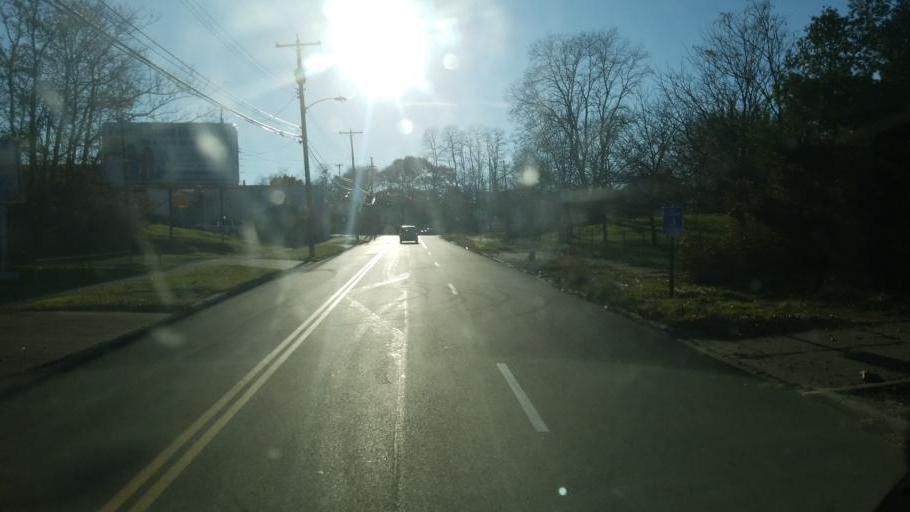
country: US
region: Ohio
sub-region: Summit County
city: Akron
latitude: 41.0684
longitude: -81.4897
